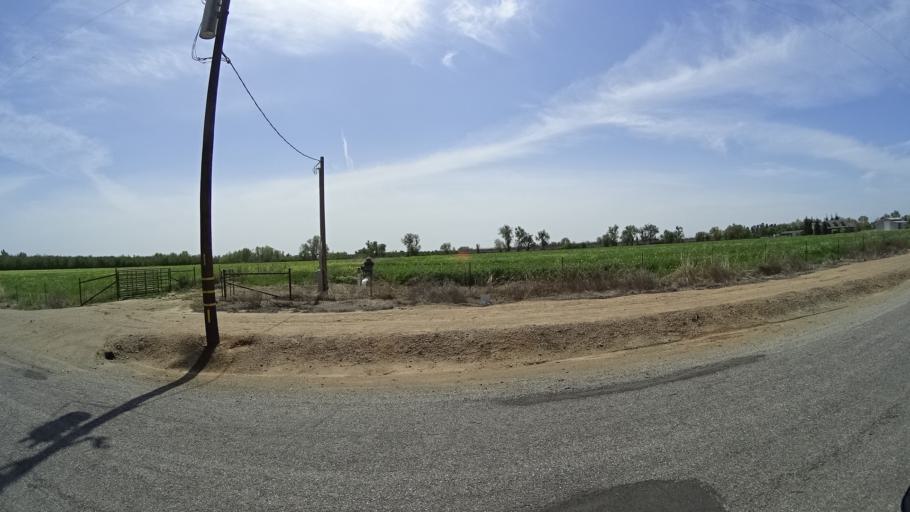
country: US
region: California
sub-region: Glenn County
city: Hamilton City
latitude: 39.7899
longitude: -122.0594
